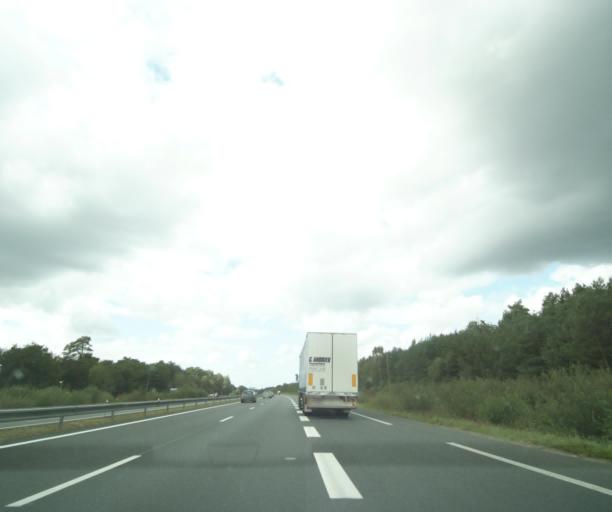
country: FR
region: Centre
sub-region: Departement du Loiret
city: La Ferte-Saint-Aubin
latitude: 47.6658
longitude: 1.9263
